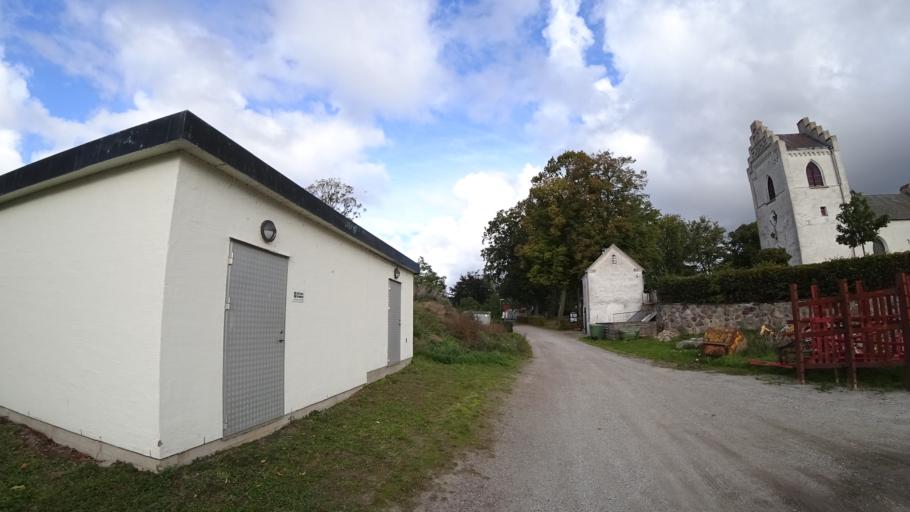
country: SE
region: Skane
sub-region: Kavlinge Kommun
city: Loddekopinge
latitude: 55.7668
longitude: 13.0555
